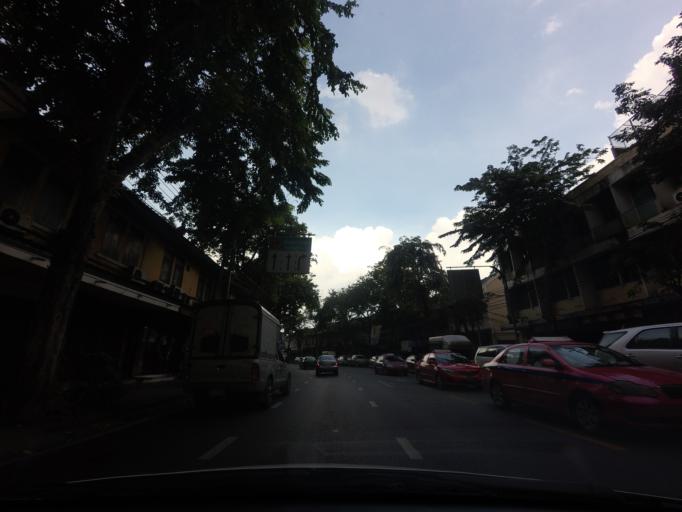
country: TH
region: Bangkok
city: Pom Prap Sattru Phai
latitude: 13.7574
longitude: 100.5097
